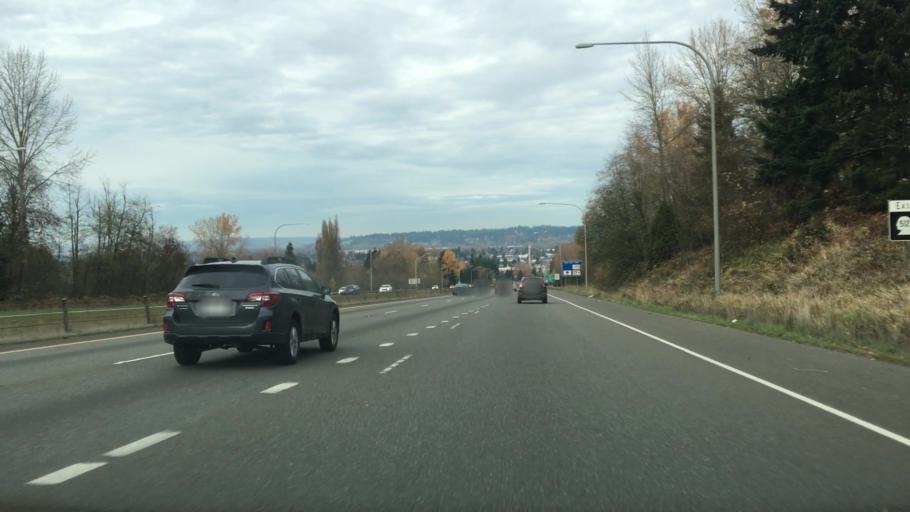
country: US
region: Washington
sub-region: Pierce County
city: Puyallup
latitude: 47.1673
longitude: -122.2965
